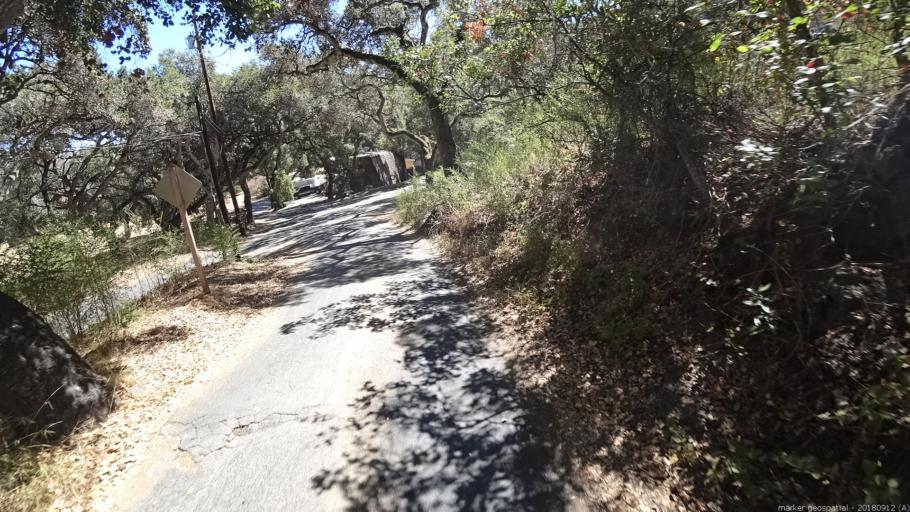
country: US
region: California
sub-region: Monterey County
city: Carmel Valley Village
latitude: 36.4676
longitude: -121.7306
